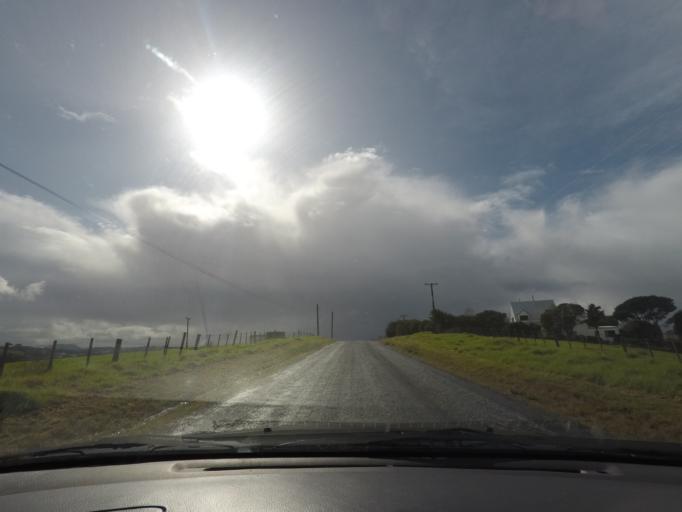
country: NZ
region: Auckland
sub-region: Auckland
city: Warkworth
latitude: -36.4308
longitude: 174.7220
